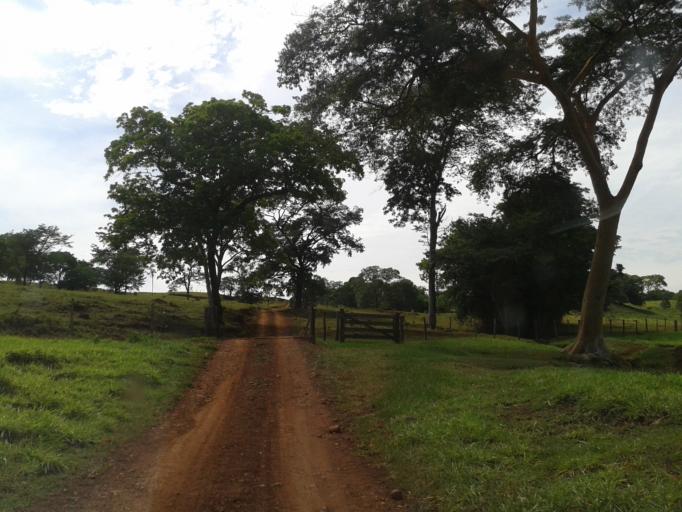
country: BR
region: Minas Gerais
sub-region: Centralina
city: Centralina
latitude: -18.6987
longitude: -49.2080
